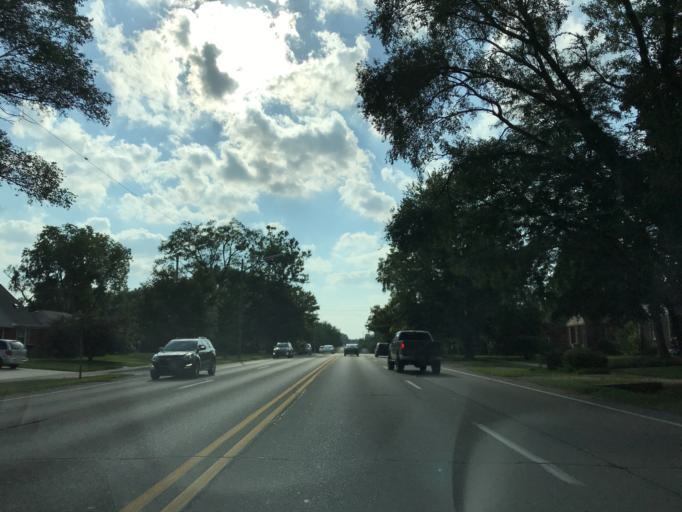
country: US
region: Michigan
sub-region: Wayne County
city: Redford
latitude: 42.3991
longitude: -83.3053
